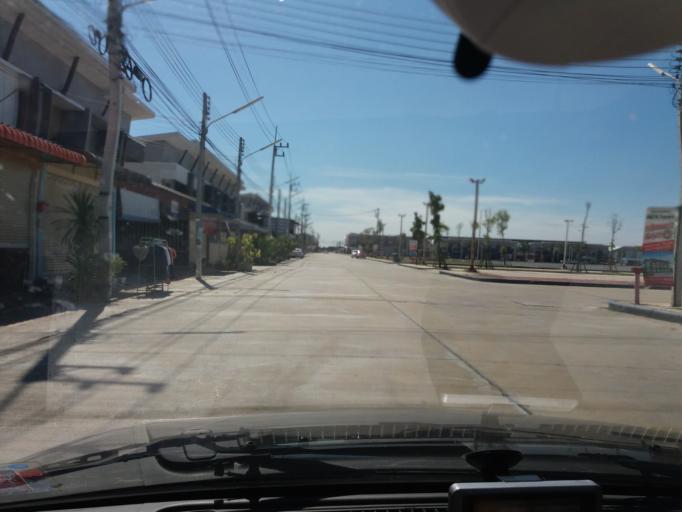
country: TH
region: Suphan Buri
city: Suphan Buri
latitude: 14.4616
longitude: 100.1464
